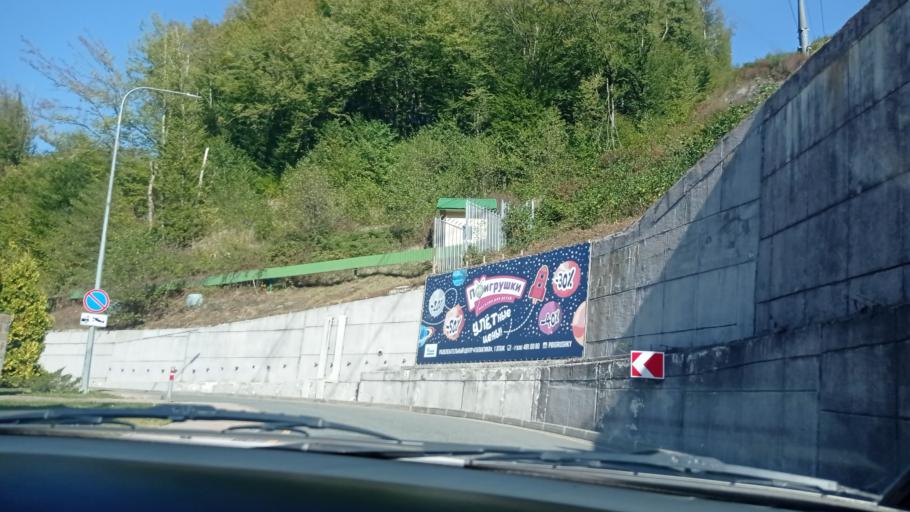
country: RU
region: Krasnodarskiy
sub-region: Sochi City
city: Krasnaya Polyana
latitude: 43.6841
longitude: 40.2812
